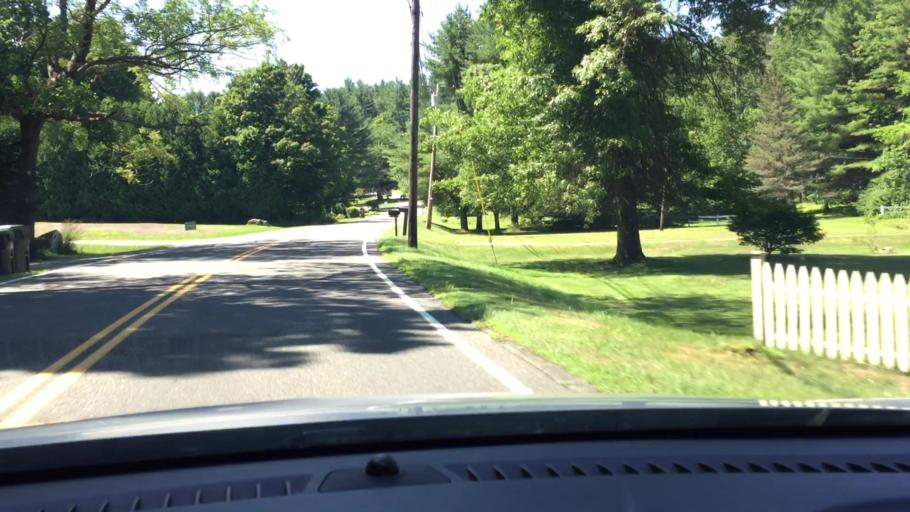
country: US
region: Massachusetts
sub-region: Berkshire County
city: Lenox
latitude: 42.3802
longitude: -73.2567
